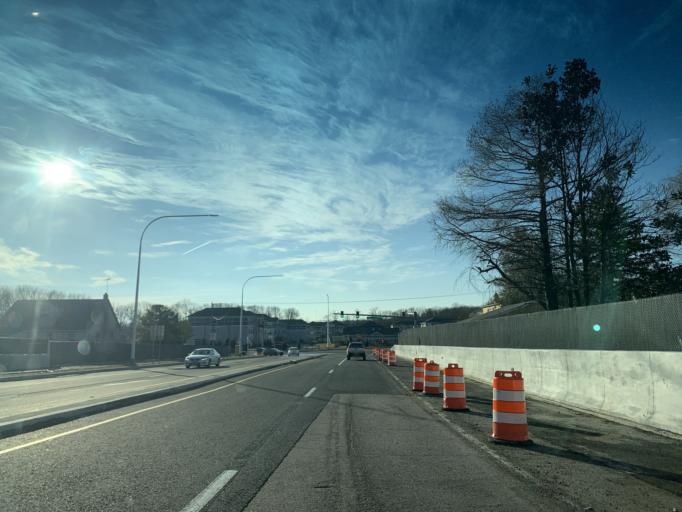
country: US
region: Delaware
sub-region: New Castle County
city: Bear
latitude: 39.6742
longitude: -75.6567
